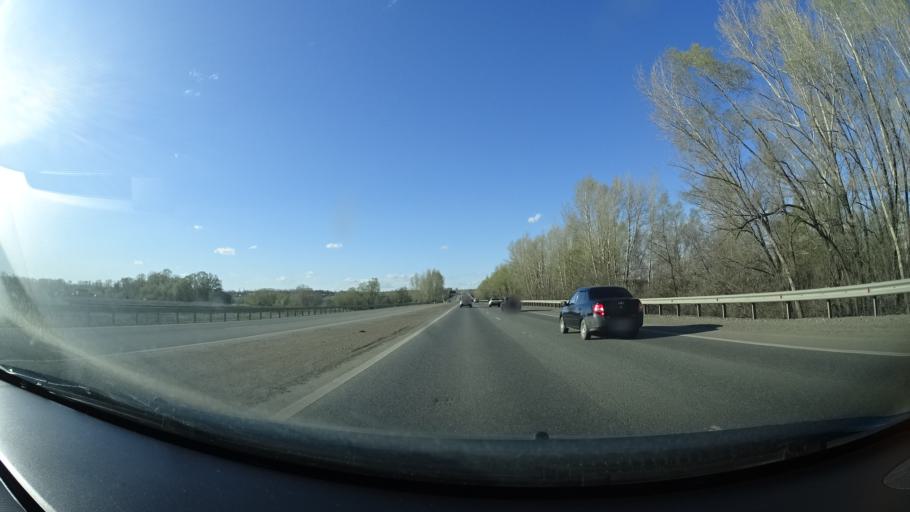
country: RU
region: Bashkortostan
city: Avdon
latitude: 54.5086
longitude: 55.9008
